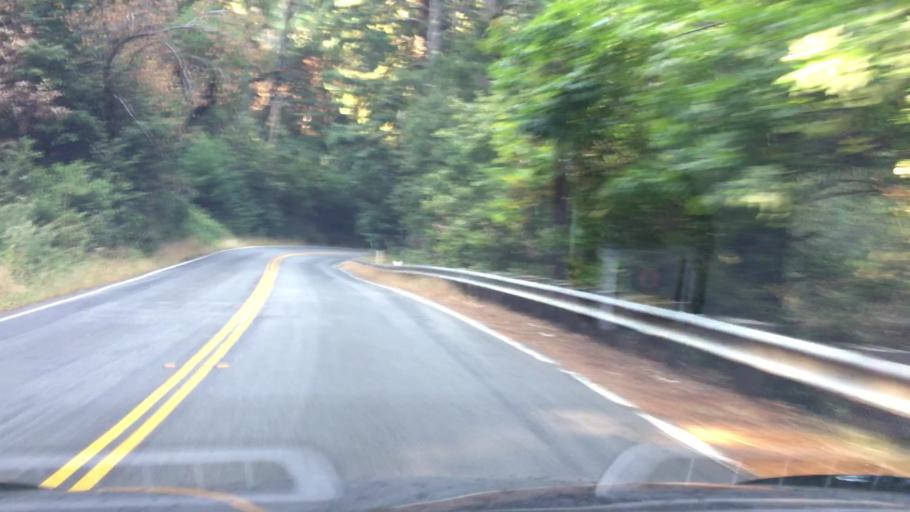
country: US
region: California
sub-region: San Mateo County
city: Woodside
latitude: 37.3923
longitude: -122.2886
